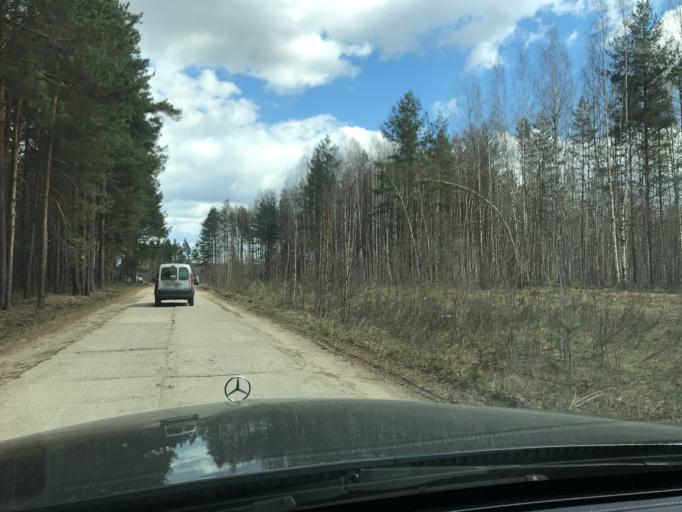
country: RU
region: Vladimir
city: Pokrov
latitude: 55.8711
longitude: 39.2380
